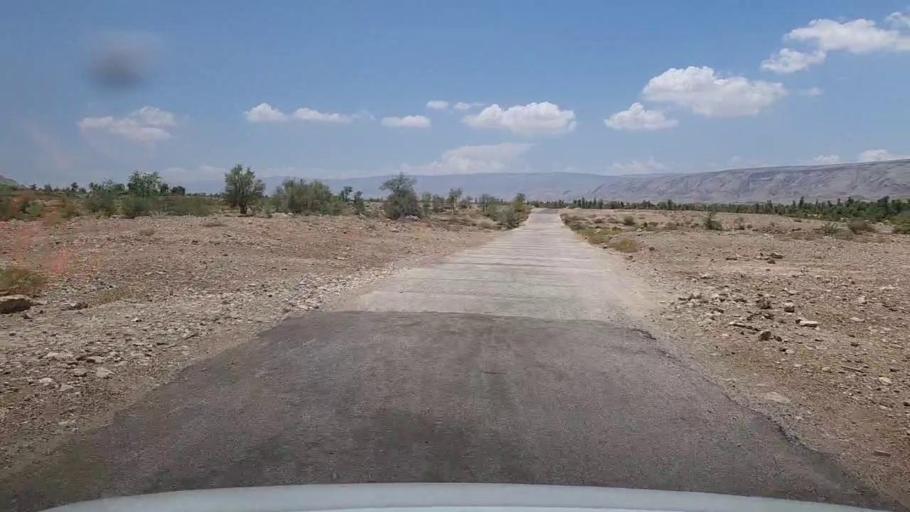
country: PK
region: Sindh
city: Bhan
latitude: 26.2855
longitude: 67.5327
